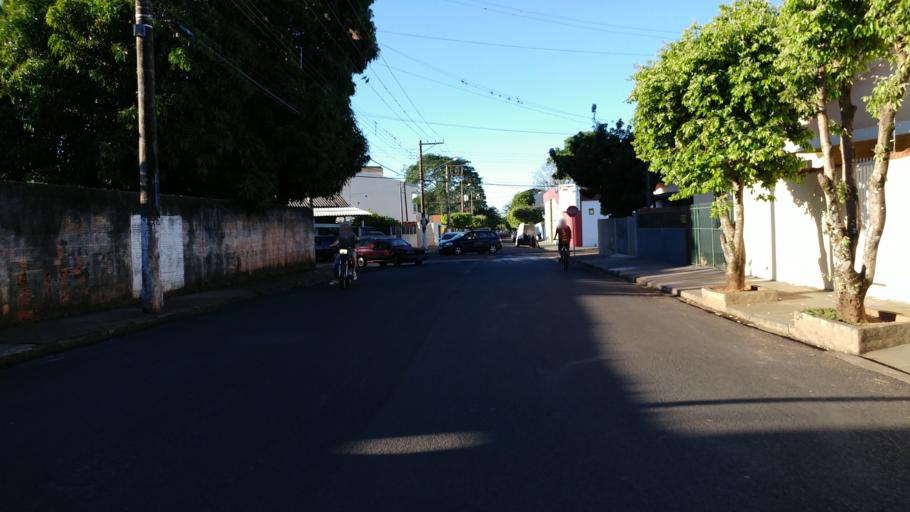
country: BR
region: Sao Paulo
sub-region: Paraguacu Paulista
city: Paraguacu Paulista
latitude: -22.4226
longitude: -50.5795
